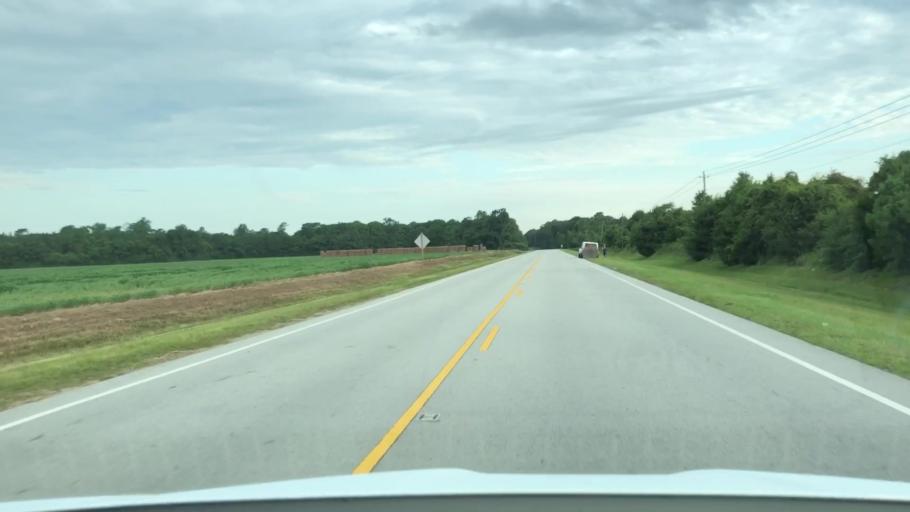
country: US
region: North Carolina
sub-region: Jones County
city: Trenton
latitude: 35.0023
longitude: -77.2756
